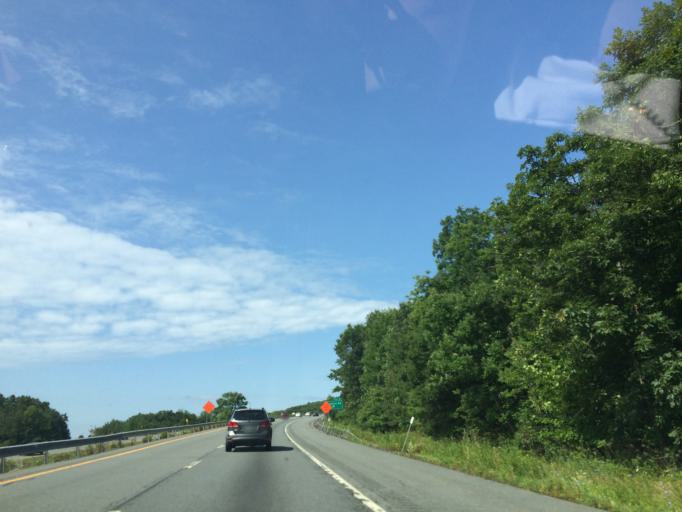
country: US
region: New York
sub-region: Orange County
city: Port Jervis
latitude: 41.3762
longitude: -74.6072
